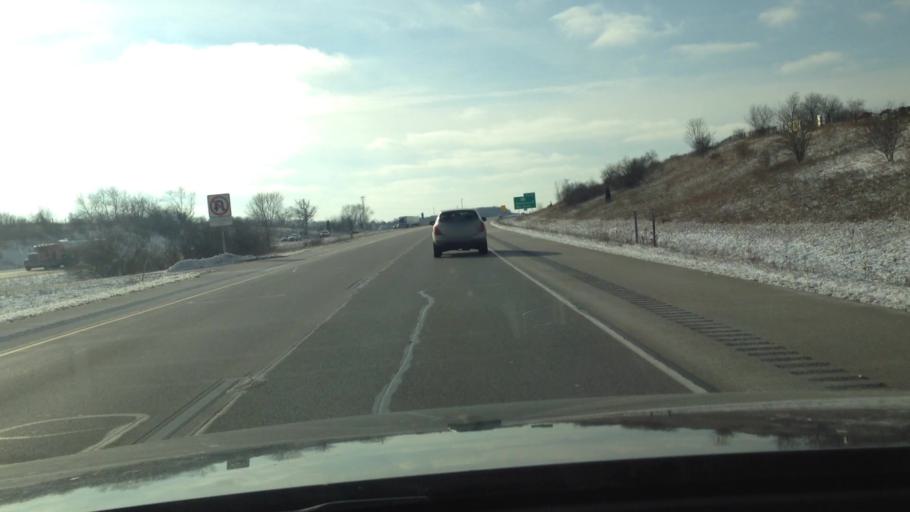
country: US
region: Wisconsin
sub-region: Waukesha County
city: Big Bend
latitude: 42.9139
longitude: -88.2092
